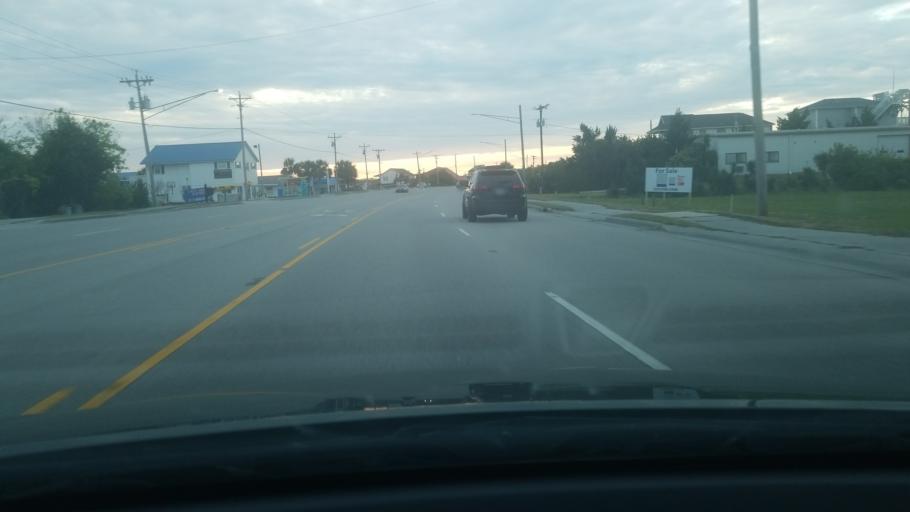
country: US
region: North Carolina
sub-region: Onslow County
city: Swansboro
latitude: 34.6774
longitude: -77.1064
